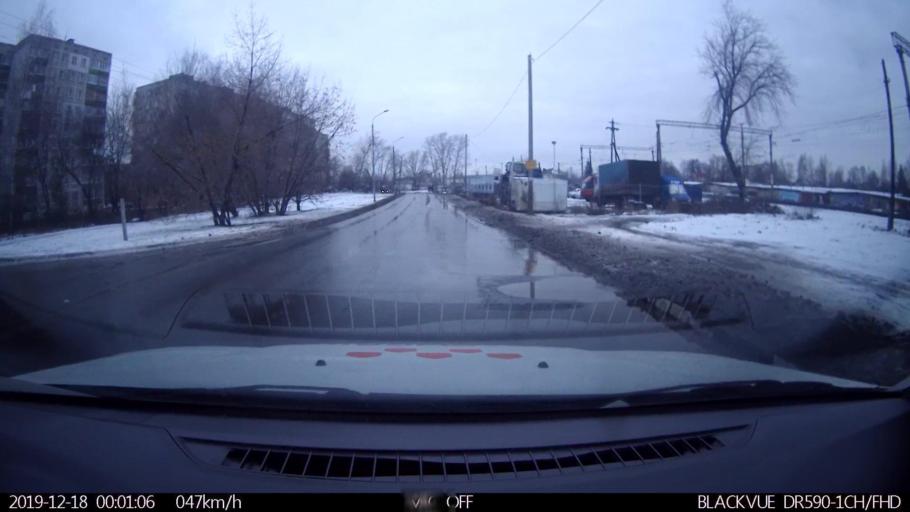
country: RU
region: Nizjnij Novgorod
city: Gorbatovka
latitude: 56.3688
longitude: 43.8260
